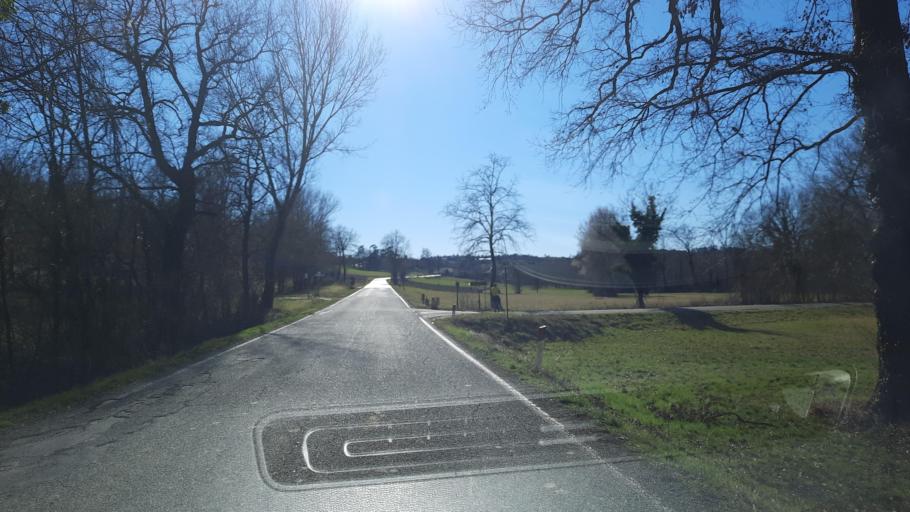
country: IT
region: Piedmont
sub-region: Provincia di Alessandria
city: Frassinello Monferrato
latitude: 45.0485
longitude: 8.3929
